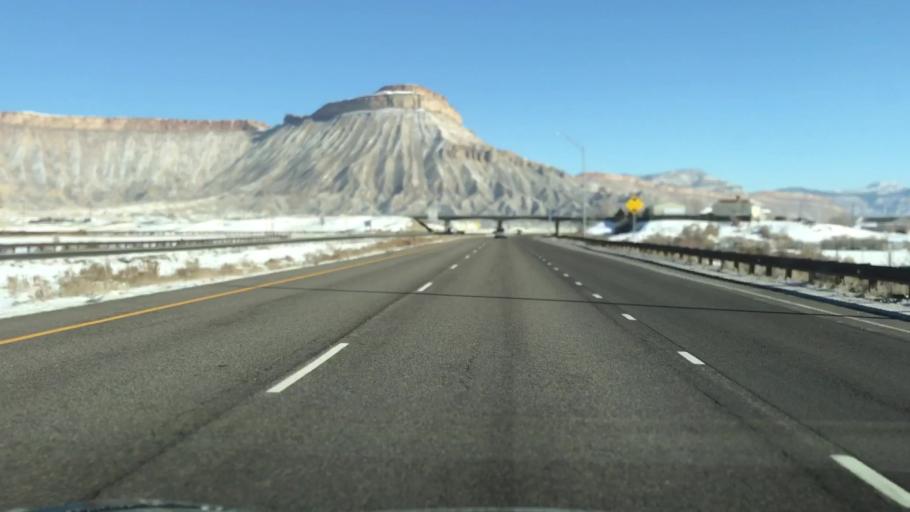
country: US
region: Colorado
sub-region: Mesa County
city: Clifton
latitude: 39.1056
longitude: -108.4439
